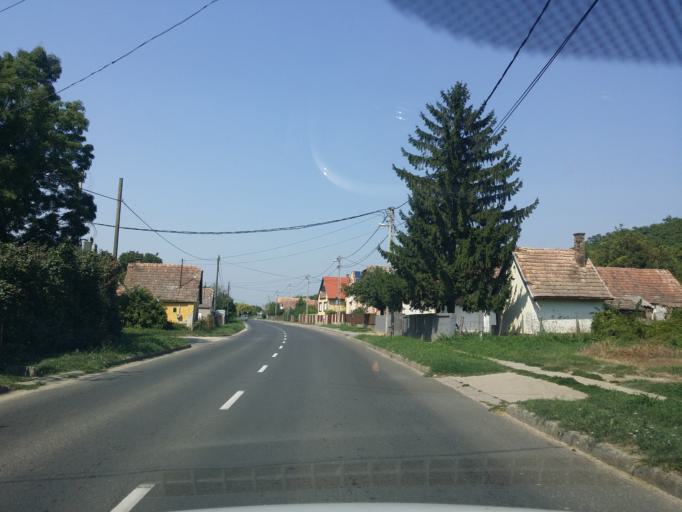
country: HU
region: Tolna
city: Pincehely
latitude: 46.7099
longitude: 18.4715
